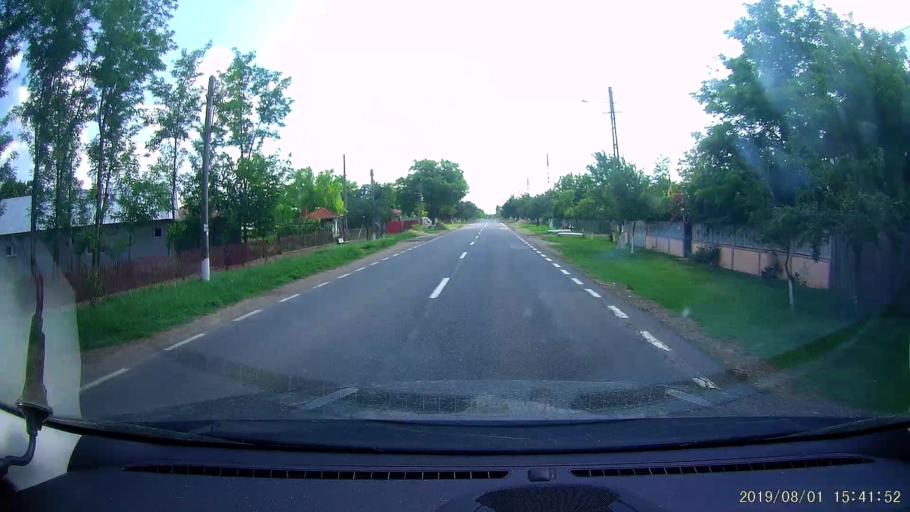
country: RO
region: Braila
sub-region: Comuna Baraganul
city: Baraganul
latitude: 44.8179
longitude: 27.5209
